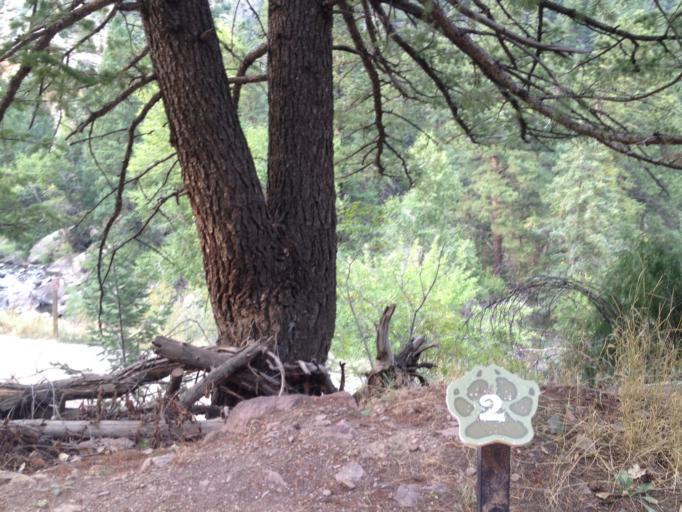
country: US
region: Colorado
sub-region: Boulder County
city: Boulder
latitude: 39.9293
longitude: -105.2896
